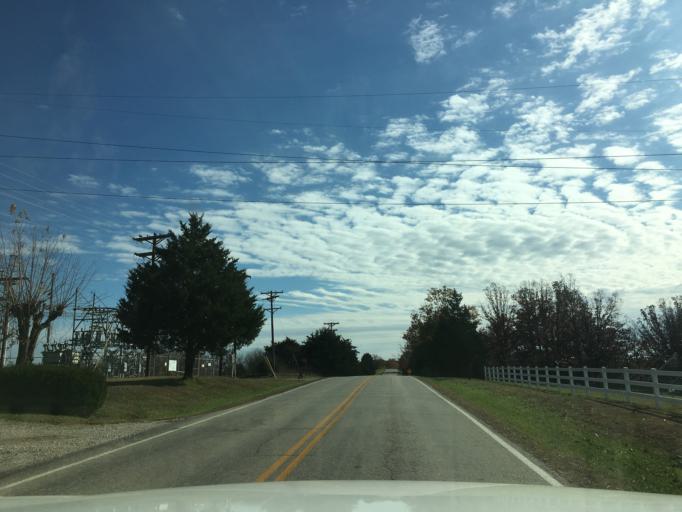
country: US
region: Missouri
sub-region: Osage County
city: Linn
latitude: 38.4287
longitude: -91.8265
